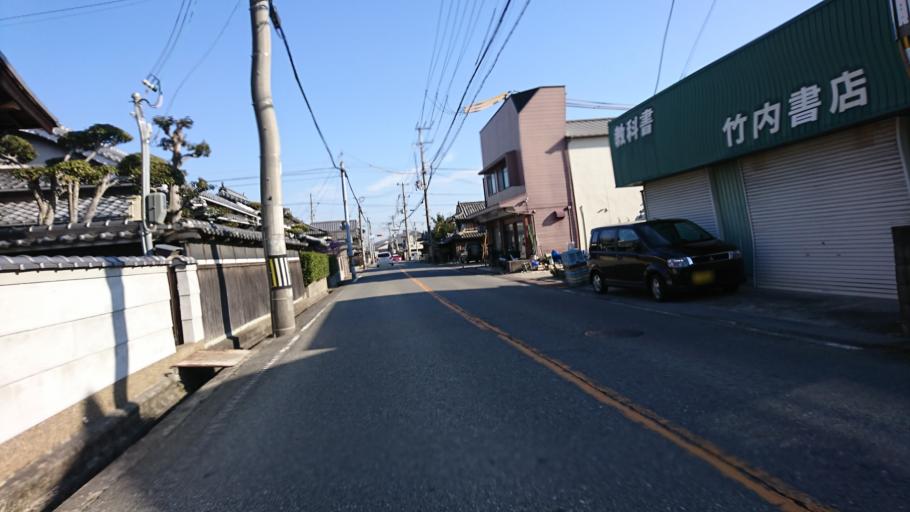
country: JP
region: Hyogo
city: Kakogawacho-honmachi
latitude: 34.8170
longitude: 134.8203
